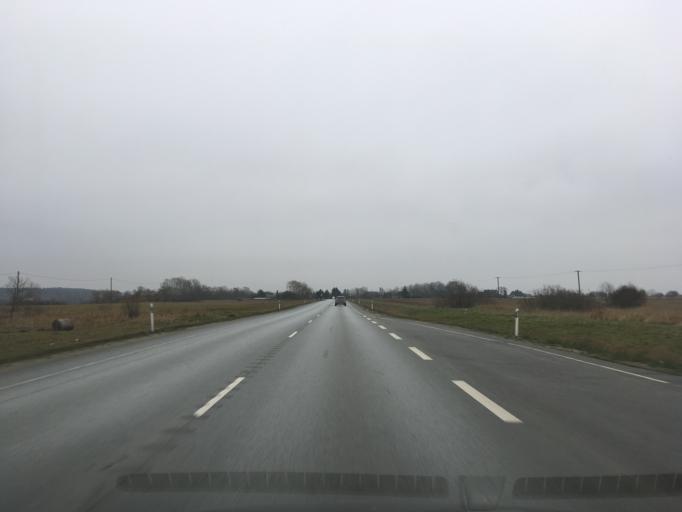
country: EE
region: Ida-Virumaa
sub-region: Kivioli linn
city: Kivioli
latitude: 59.4138
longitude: 26.9853
